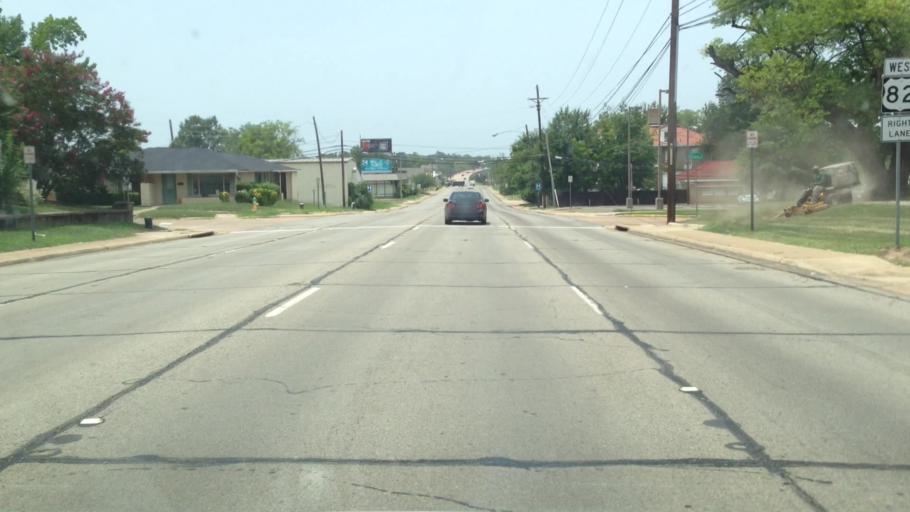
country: US
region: Texas
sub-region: Bowie County
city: Texarkana
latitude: 33.4277
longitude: -94.0447
